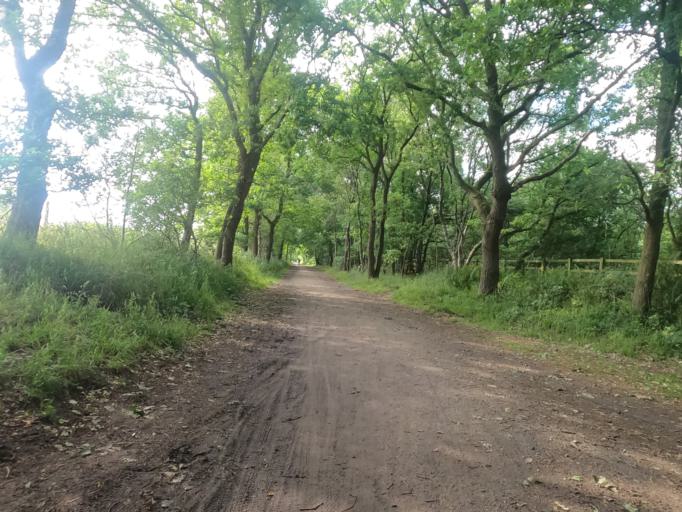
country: GB
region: England
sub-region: Cheshire West and Chester
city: Cuddington
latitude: 53.2127
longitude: -2.5937
